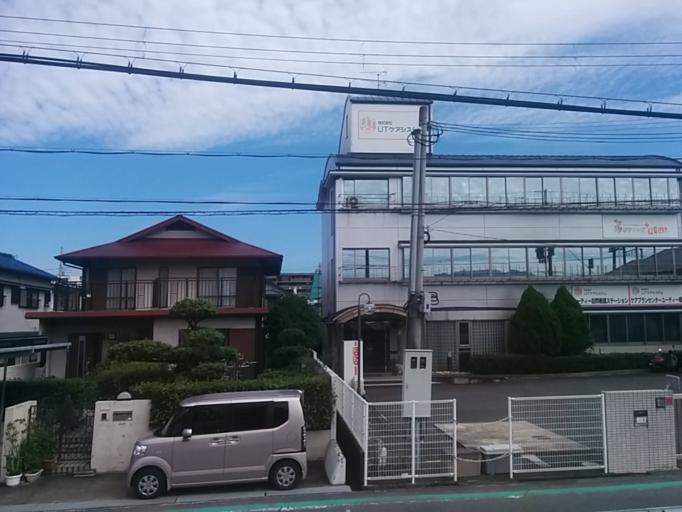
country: JP
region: Nara
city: Kashihara-shi
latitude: 34.4889
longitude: 135.7945
